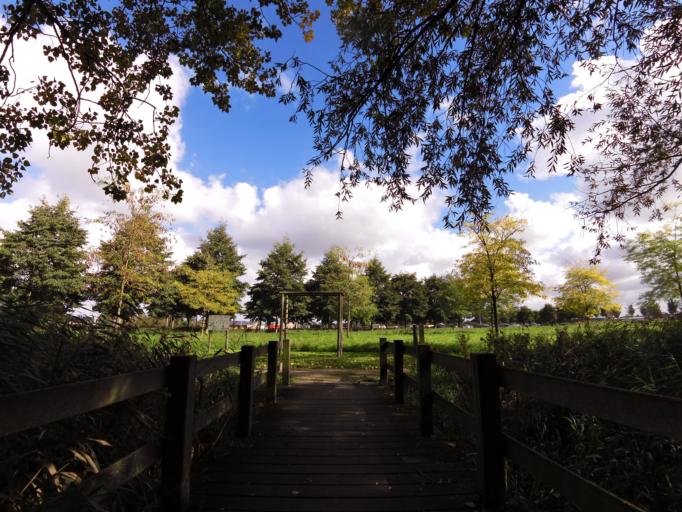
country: BE
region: Flanders
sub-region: Provincie West-Vlaanderen
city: Ostend
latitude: 51.2009
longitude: 2.9236
